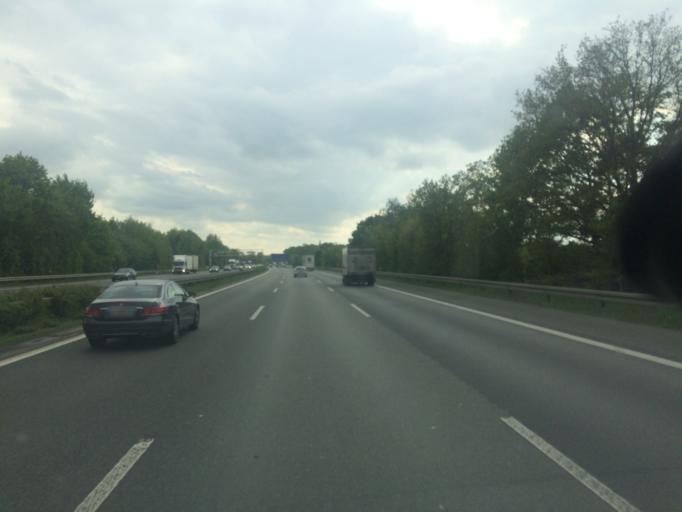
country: DE
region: North Rhine-Westphalia
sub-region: Regierungsbezirk Detmold
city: Guetersloh
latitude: 51.8910
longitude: 8.4469
